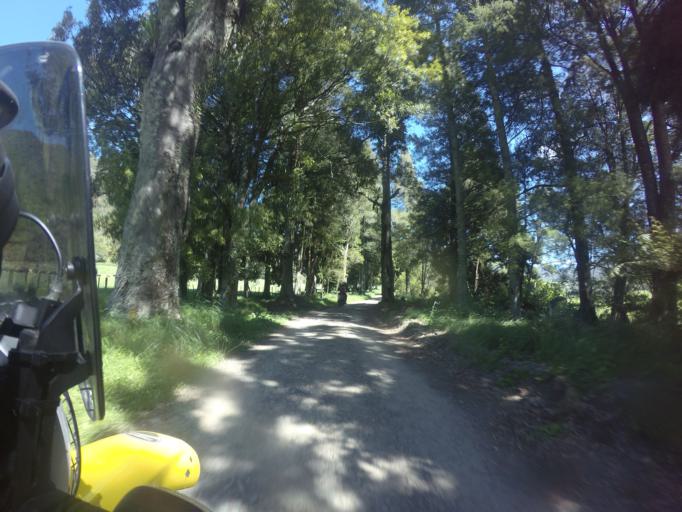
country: NZ
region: Bay of Plenty
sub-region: Opotiki District
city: Opotiki
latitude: -38.2999
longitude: 177.3347
